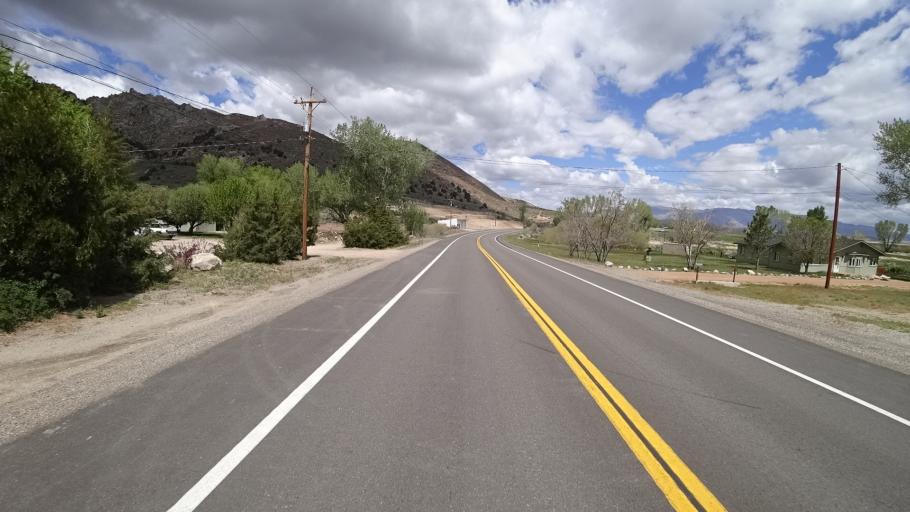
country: US
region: Nevada
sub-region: Lyon County
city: Smith Valley
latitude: 38.6240
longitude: -119.5230
